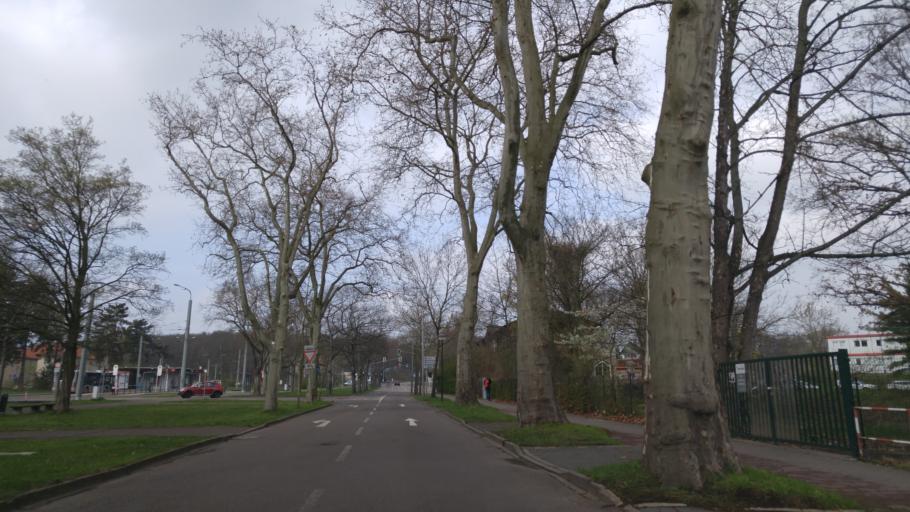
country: DE
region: Saxony-Anhalt
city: Halle Neustadt
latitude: 51.4995
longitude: 11.9343
